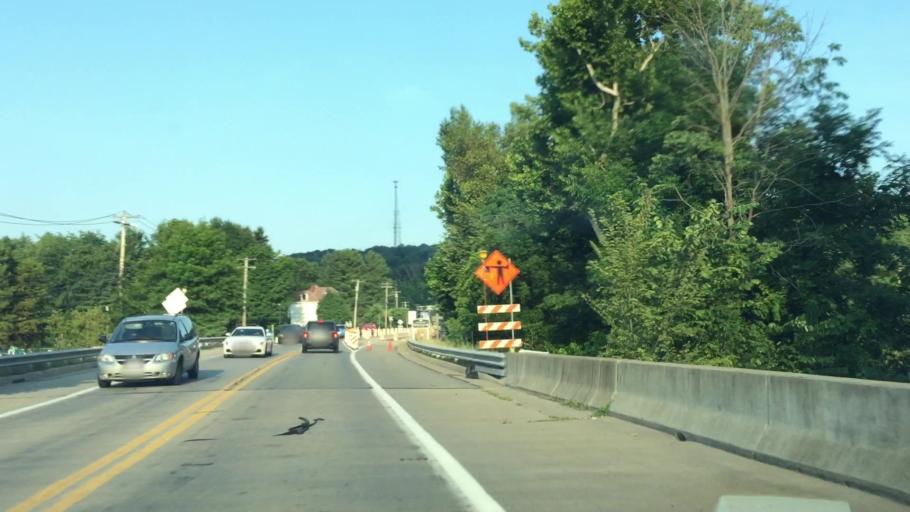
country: US
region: Pennsylvania
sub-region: Washington County
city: Thompsonville
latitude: 40.3188
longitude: -80.1158
